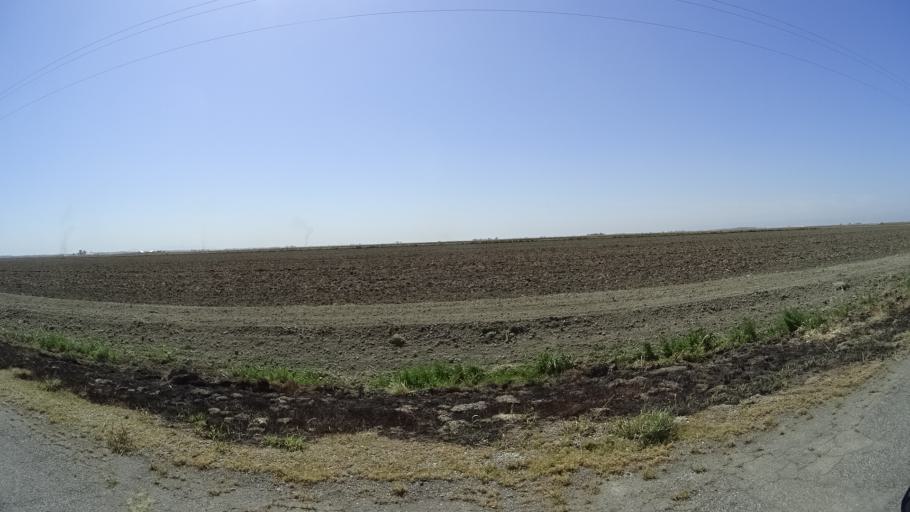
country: US
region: California
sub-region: Glenn County
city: Willows
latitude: 39.4928
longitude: -122.0689
